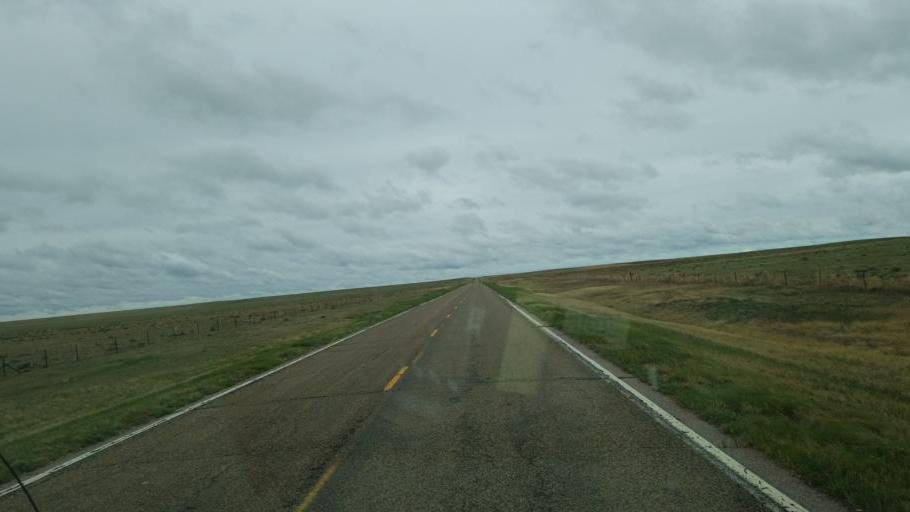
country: US
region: Colorado
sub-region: Lincoln County
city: Hugo
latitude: 38.8501
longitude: -103.4284
